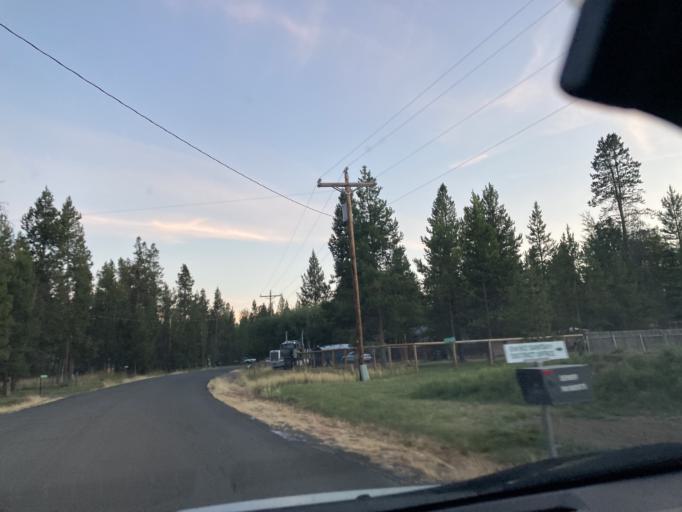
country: US
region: Oregon
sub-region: Deschutes County
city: Three Rivers
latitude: 43.8281
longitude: -121.4644
